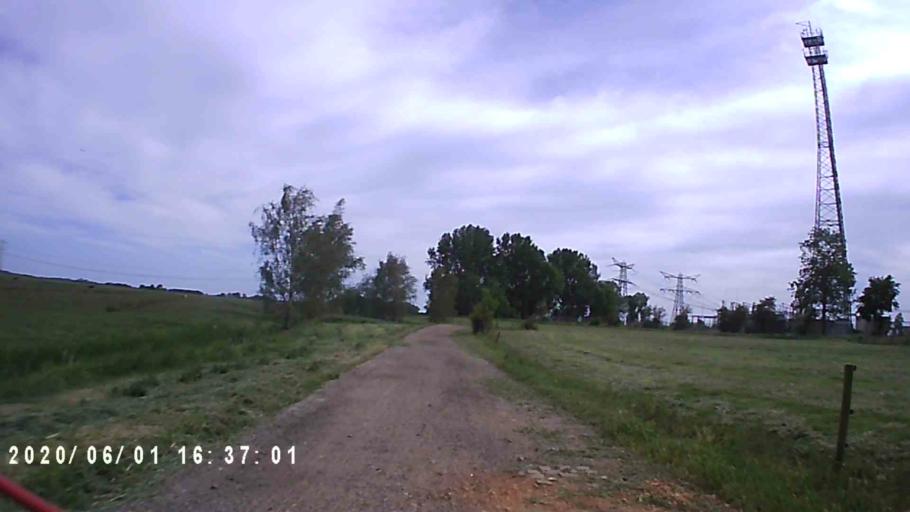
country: NL
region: Friesland
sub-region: Gemeente Tytsjerksteradiel
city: Tytsjerk
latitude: 53.1915
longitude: 5.8777
